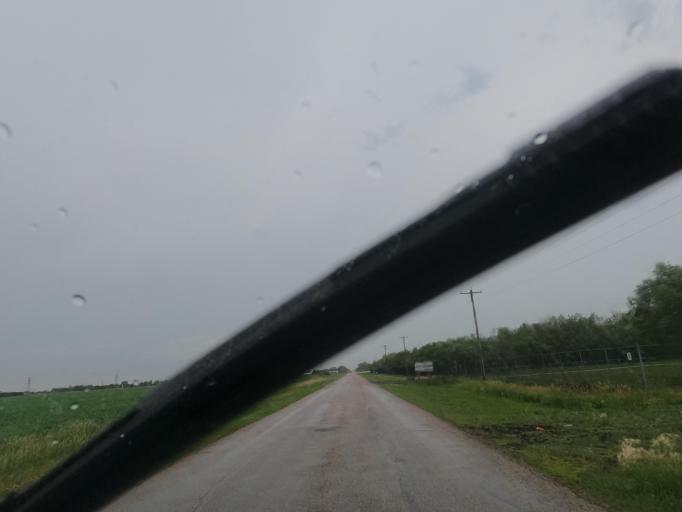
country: CA
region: Manitoba
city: Winnipeg
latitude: 49.8342
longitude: -96.9812
